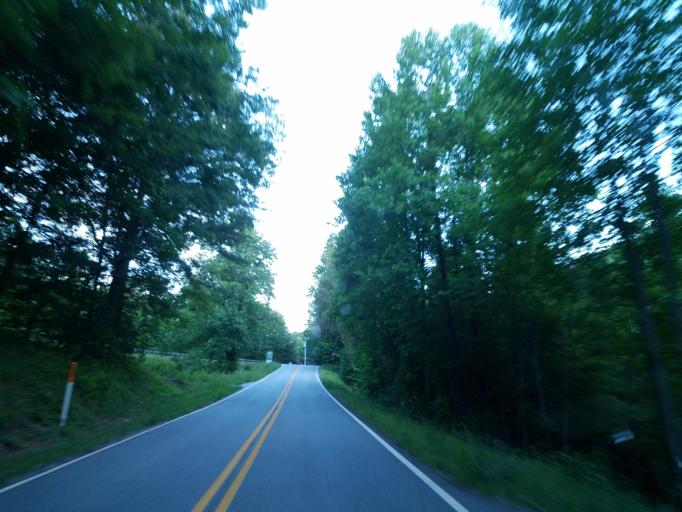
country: US
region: Georgia
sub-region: Lumpkin County
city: Dahlonega
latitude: 34.5896
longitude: -83.9714
